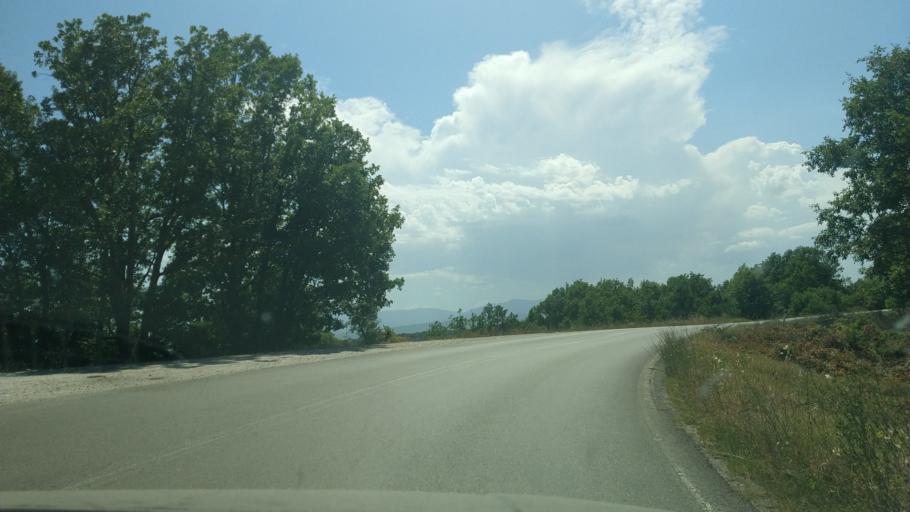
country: GR
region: West Macedonia
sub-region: Nomos Grevenon
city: Grevena
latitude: 40.0665
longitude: 21.4563
